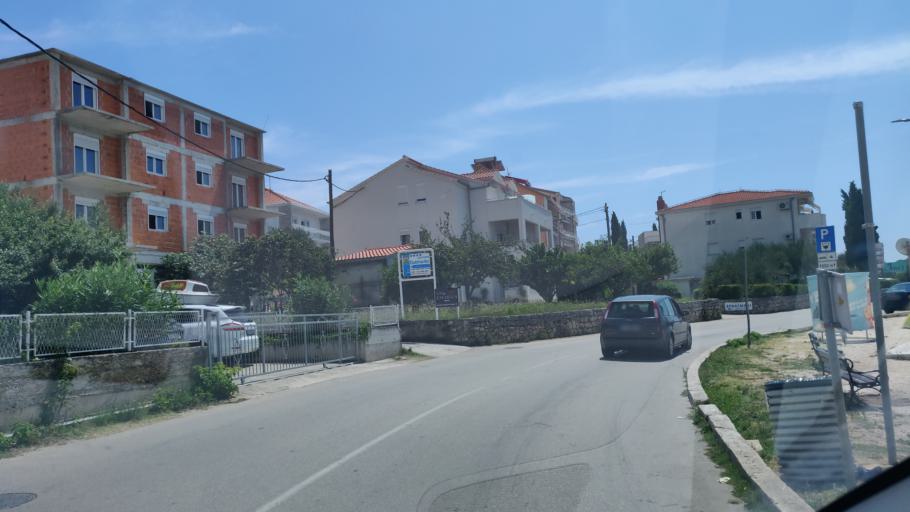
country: HR
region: Splitsko-Dalmatinska
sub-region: Grad Trogir
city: Trogir
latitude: 43.5025
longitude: 16.2596
